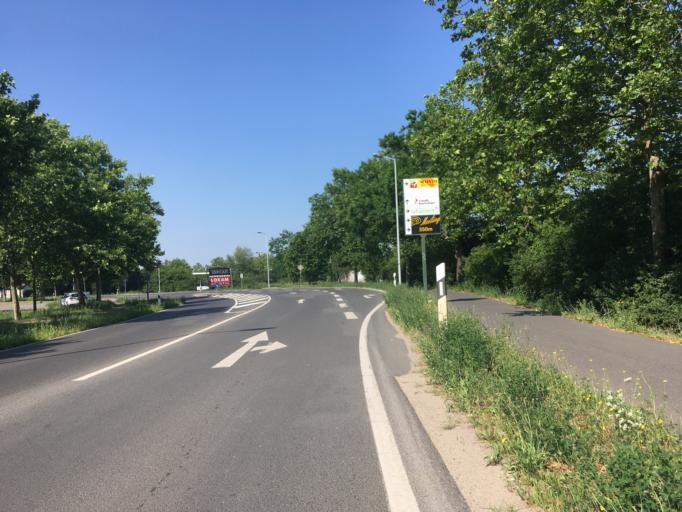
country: DE
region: Saxony-Anhalt
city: Dessau
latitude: 51.8166
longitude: 12.2263
